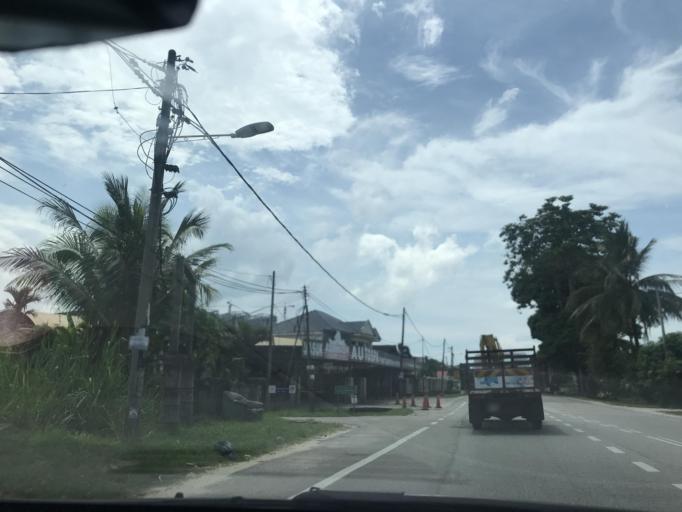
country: MY
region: Kelantan
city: Kota Bharu
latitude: 6.0970
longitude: 102.2306
